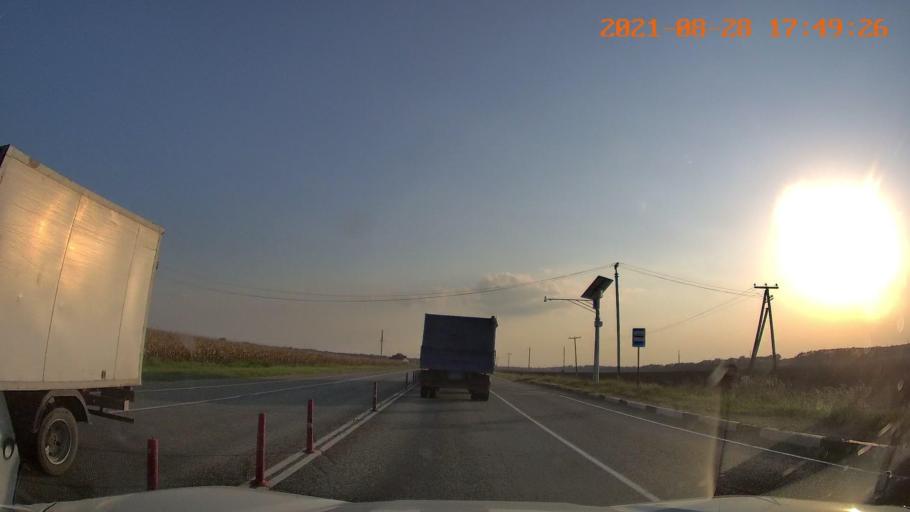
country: RU
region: Krasnodarskiy
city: Konstantinovskaya
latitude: 44.9565
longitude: 40.8289
